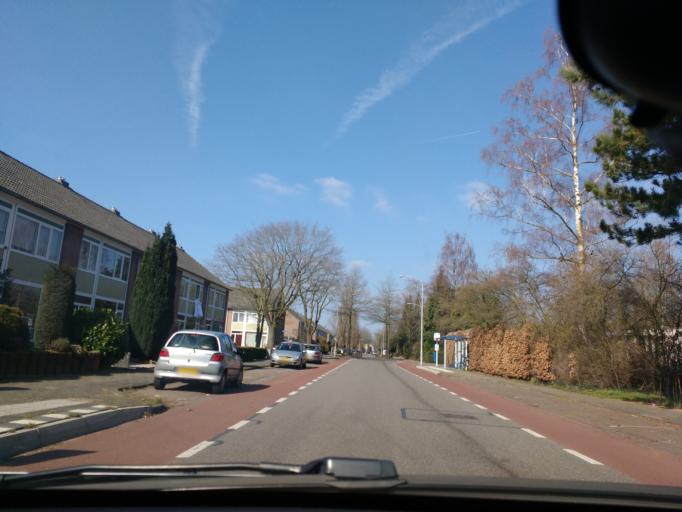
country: NL
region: North Brabant
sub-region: Gemeente Cuijk
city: Cuijk
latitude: 51.7840
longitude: 5.8595
